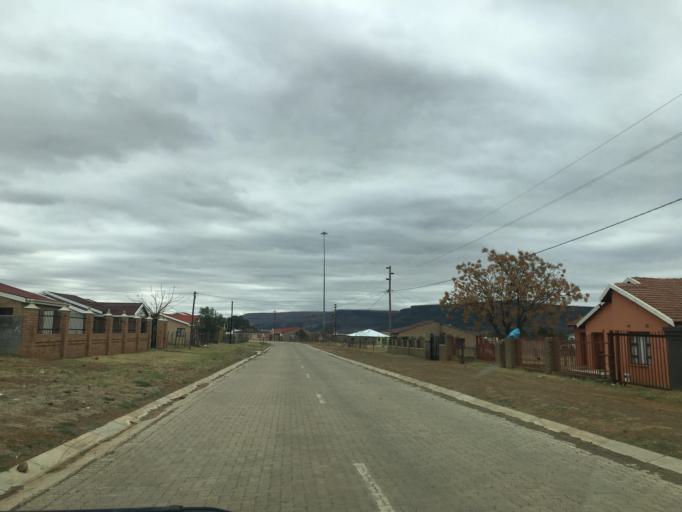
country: ZA
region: Eastern Cape
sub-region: Chris Hani District Municipality
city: Cala
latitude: -31.5359
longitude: 27.6947
